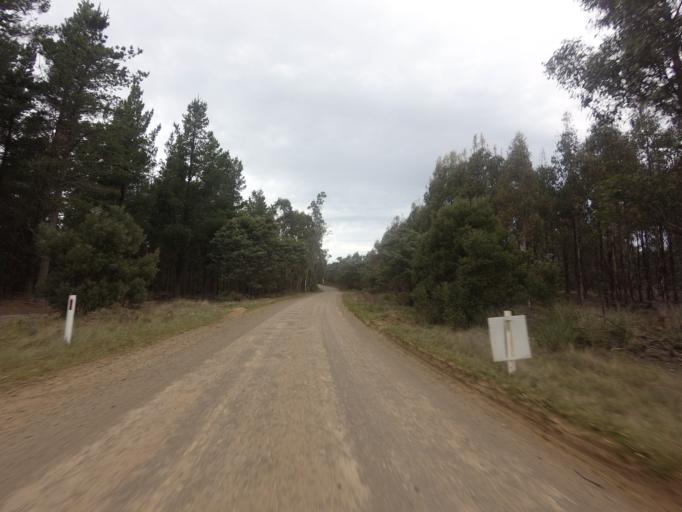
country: AU
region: Tasmania
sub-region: Derwent Valley
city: New Norfolk
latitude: -42.5725
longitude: 146.9972
